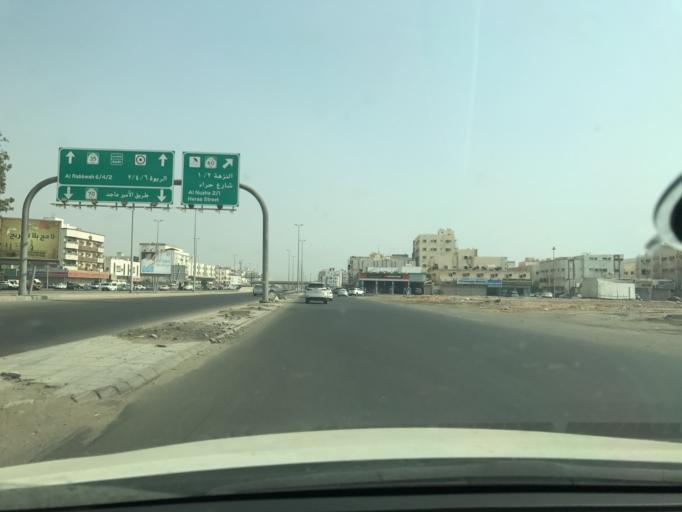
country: SA
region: Makkah
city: Jeddah
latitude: 21.6248
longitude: 39.1840
